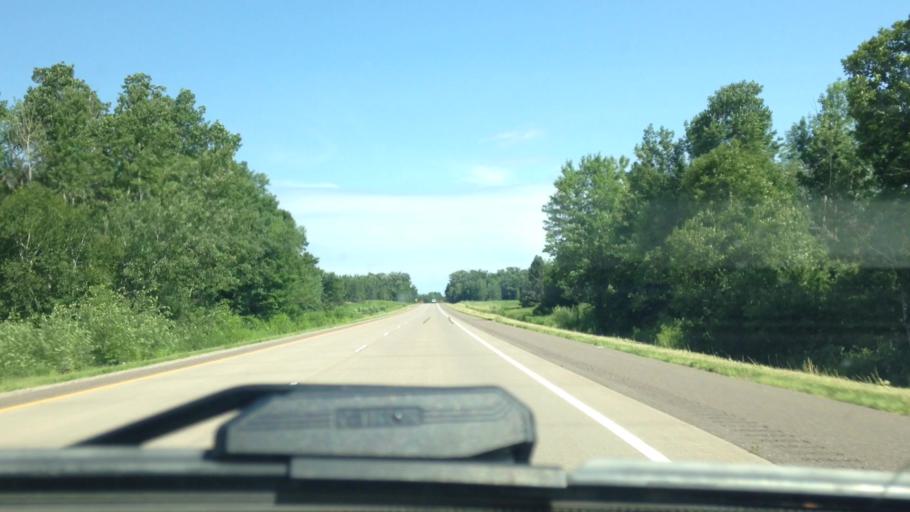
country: US
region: Wisconsin
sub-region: Barron County
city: Rice Lake
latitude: 45.5468
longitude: -91.7630
